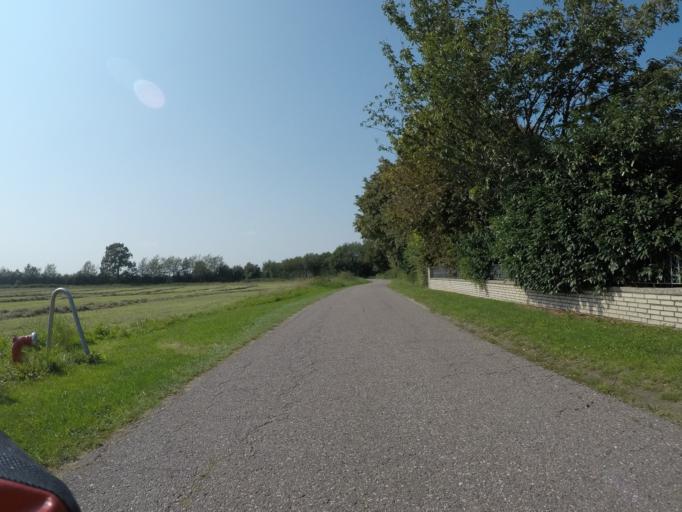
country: DE
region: Schleswig-Holstein
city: Stuvenborn
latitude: 53.8568
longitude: 10.1430
